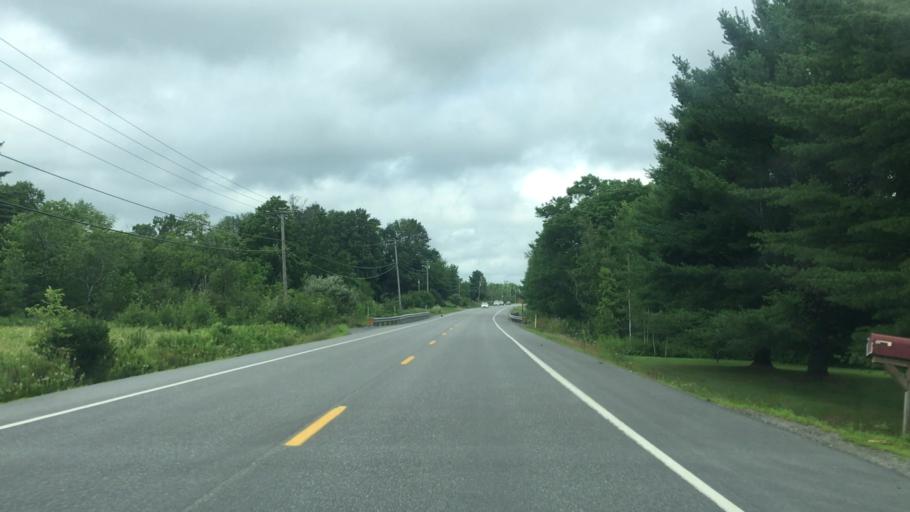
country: US
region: Maine
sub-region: Kennebec County
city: Pittston
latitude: 44.2091
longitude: -69.7548
